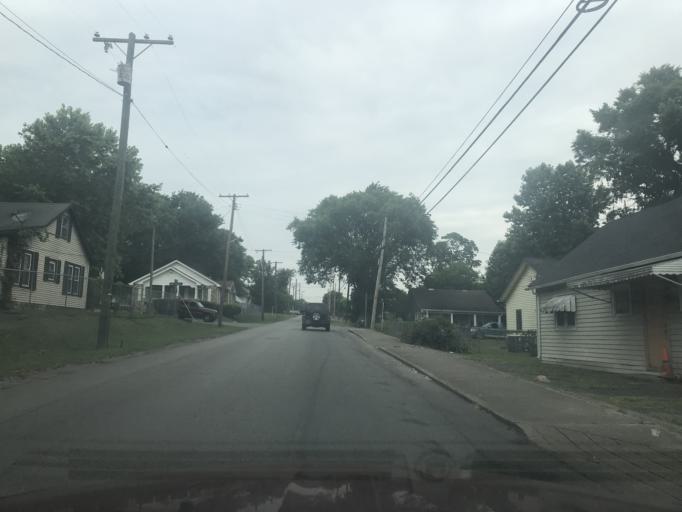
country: US
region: Tennessee
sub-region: Davidson County
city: Nashville
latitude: 36.1807
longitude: -86.8146
